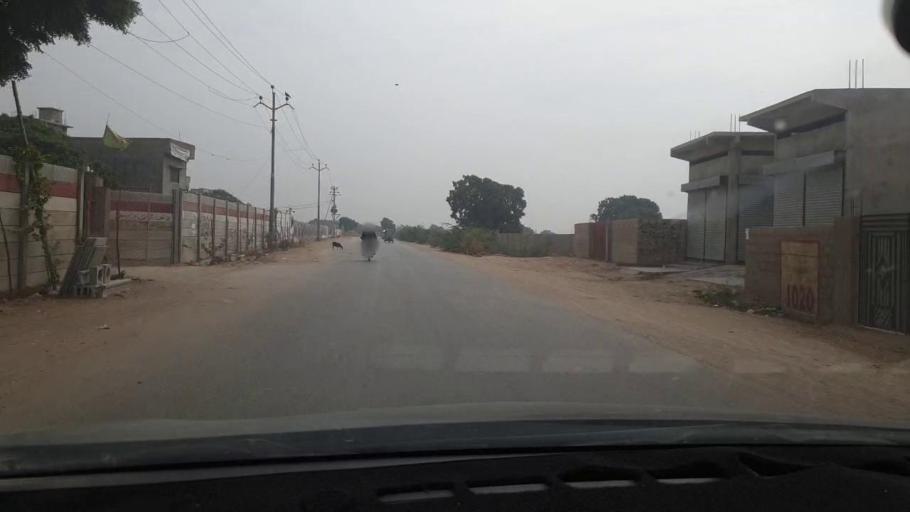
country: PK
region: Sindh
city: Malir Cantonment
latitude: 24.9181
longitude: 67.2589
